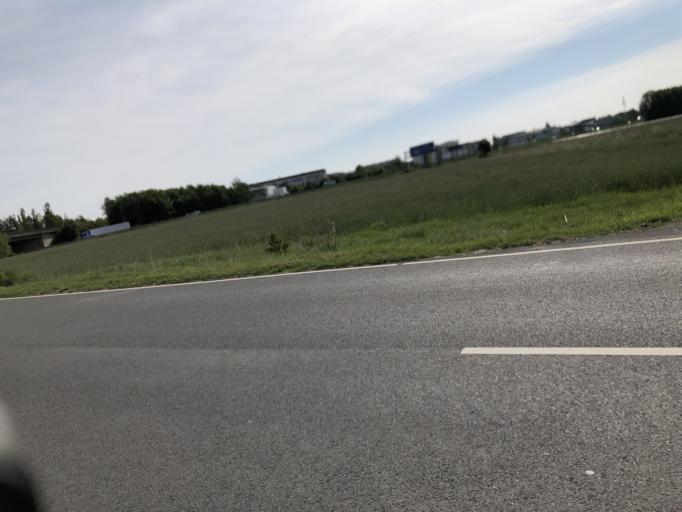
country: DE
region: Bavaria
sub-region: Regierungsbezirk Mittelfranken
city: Erlangen
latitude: 49.5432
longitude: 11.0152
